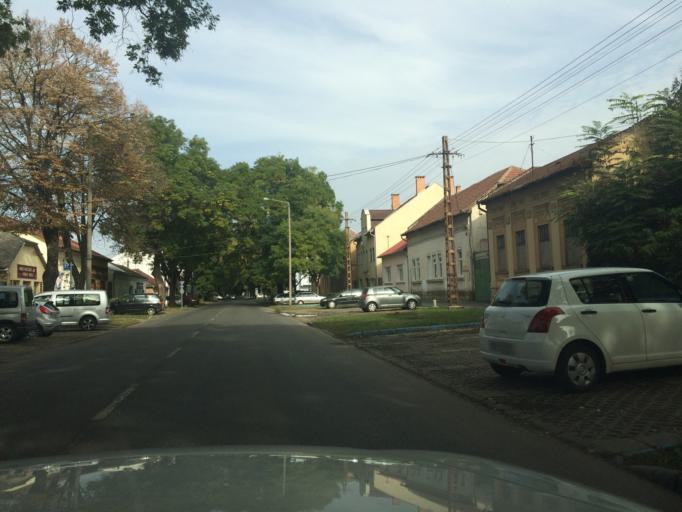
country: HU
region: Szabolcs-Szatmar-Bereg
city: Nyiregyhaza
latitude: 47.9486
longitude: 21.7157
